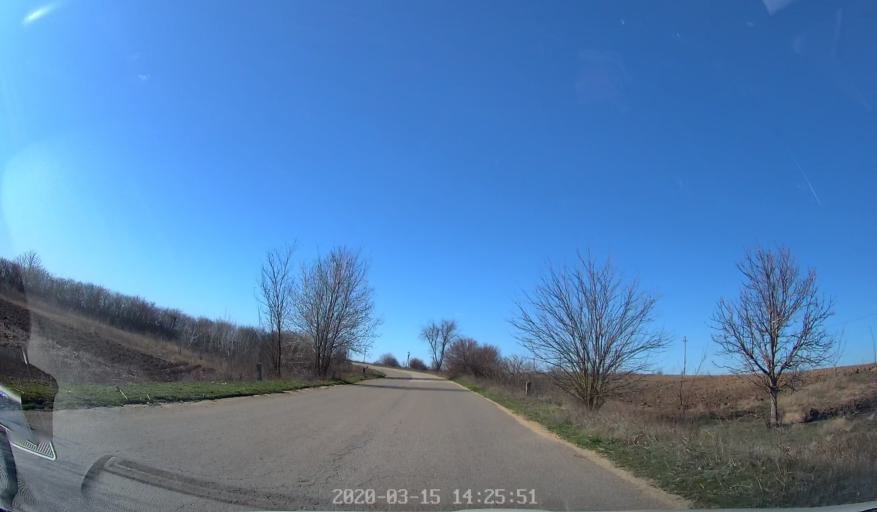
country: MD
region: Orhei
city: Orhei
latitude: 47.3414
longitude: 28.9141
